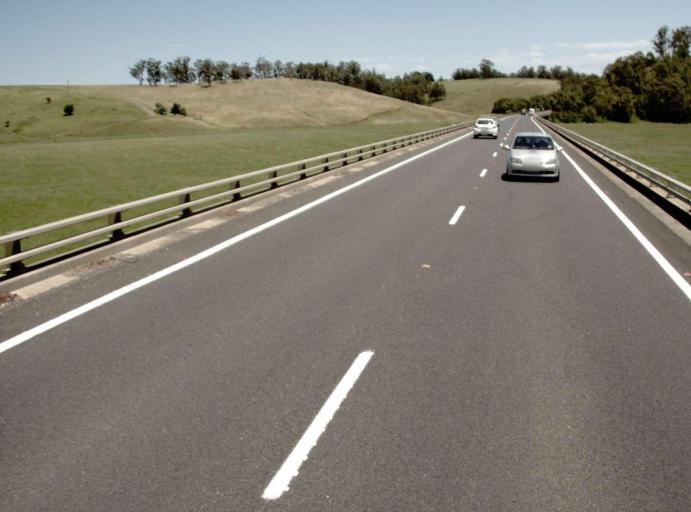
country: AU
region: Victoria
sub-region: East Gippsland
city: Lakes Entrance
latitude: -37.7255
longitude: 148.4478
